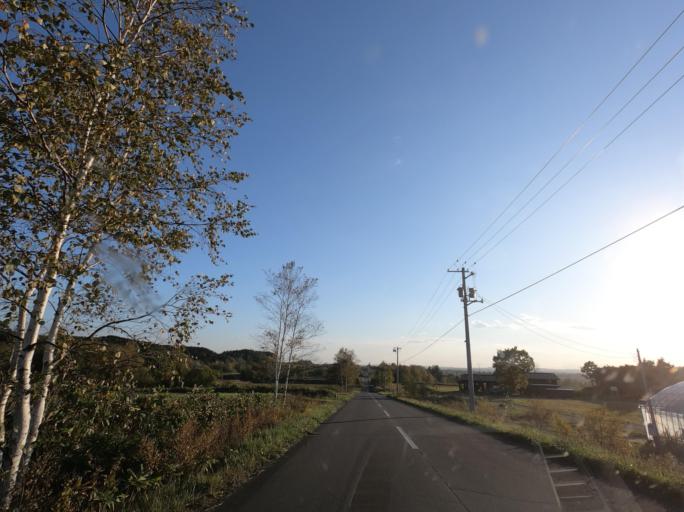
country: JP
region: Hokkaido
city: Iwamizawa
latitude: 43.0090
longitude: 141.8805
